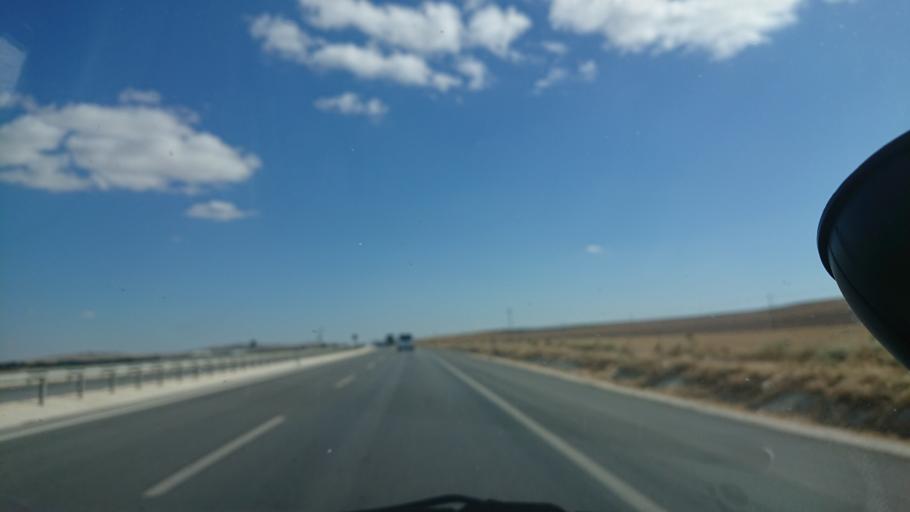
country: TR
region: Eskisehir
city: Mahmudiye
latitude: 39.5311
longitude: 30.9484
